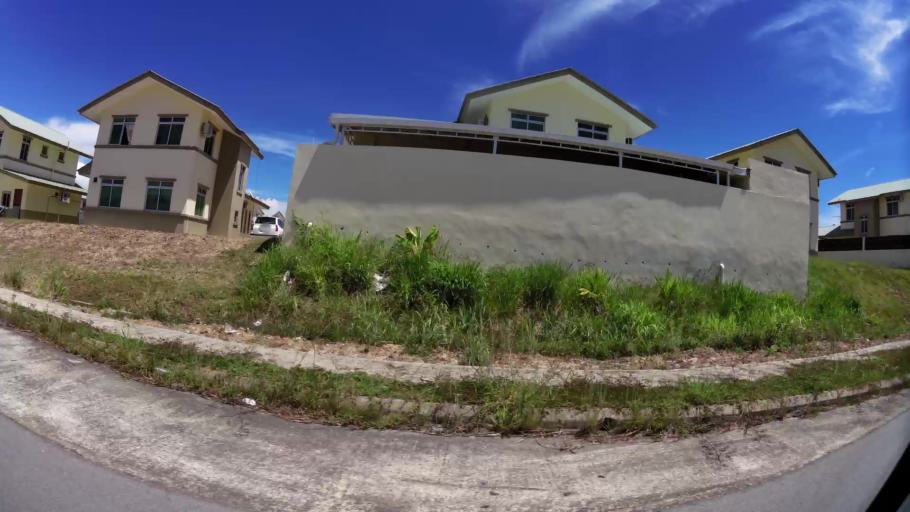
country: BN
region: Brunei and Muara
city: Bandar Seri Begawan
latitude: 5.0306
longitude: 115.0312
